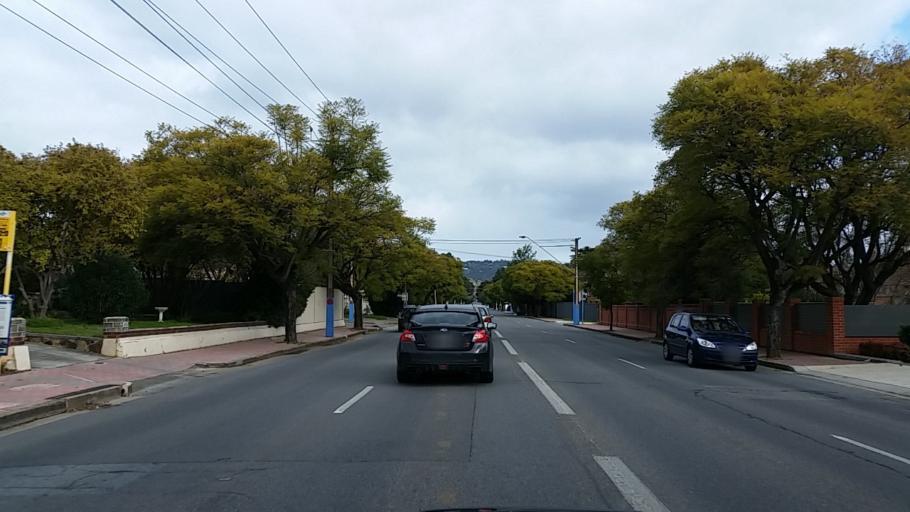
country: AU
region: South Australia
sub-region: Unley
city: Fullarton
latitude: -34.9614
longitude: 138.6262
